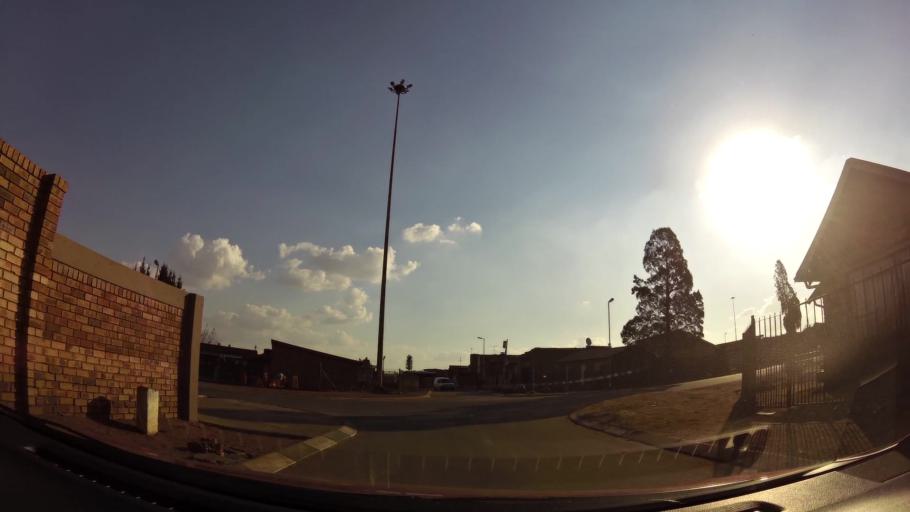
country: ZA
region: Gauteng
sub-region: City of Johannesburg Metropolitan Municipality
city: Soweto
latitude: -26.2382
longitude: 27.8566
